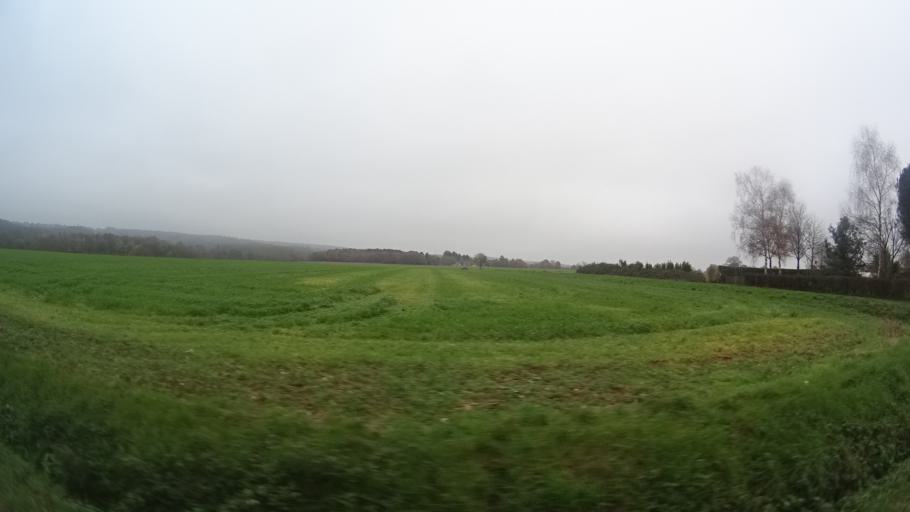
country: FR
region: Brittany
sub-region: Departement d'Ille-et-Vilaine
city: Sainte-Marie
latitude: 47.7058
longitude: -1.9935
